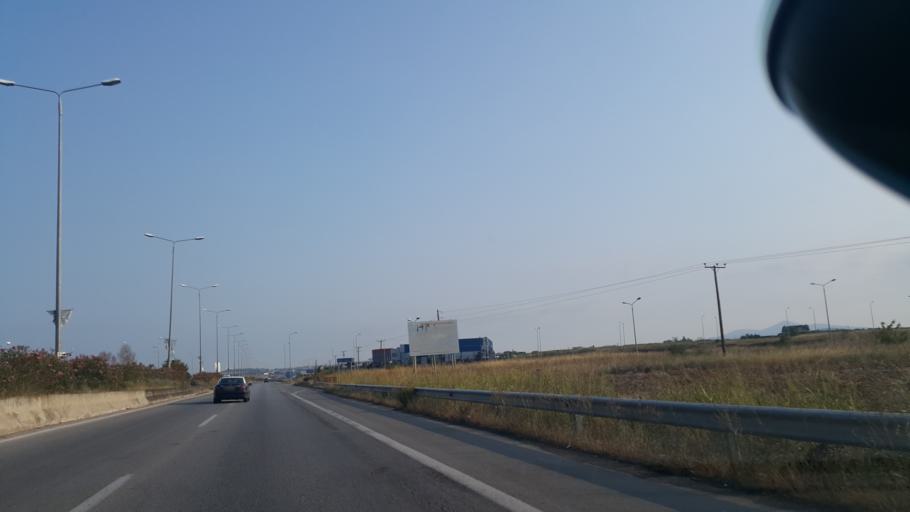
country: GR
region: Central Macedonia
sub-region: Nomos Chalkidikis
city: Lakkoma
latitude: 40.3953
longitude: 23.0335
